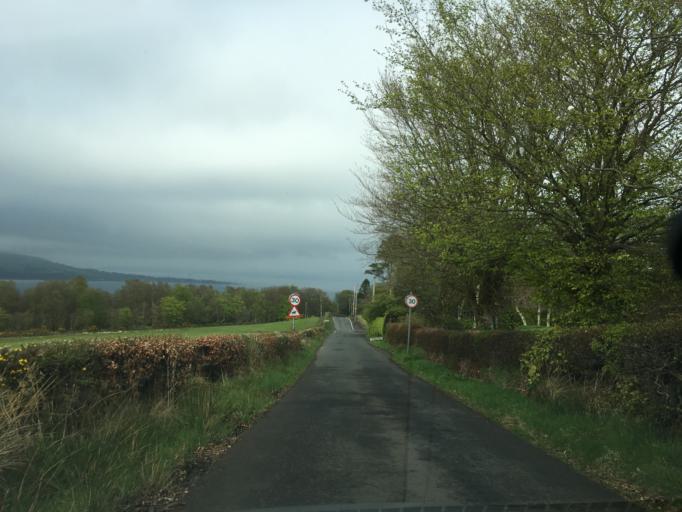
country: GB
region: Scotland
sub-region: Argyll and Bute
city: Rothesay
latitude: 55.8386
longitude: -5.0337
